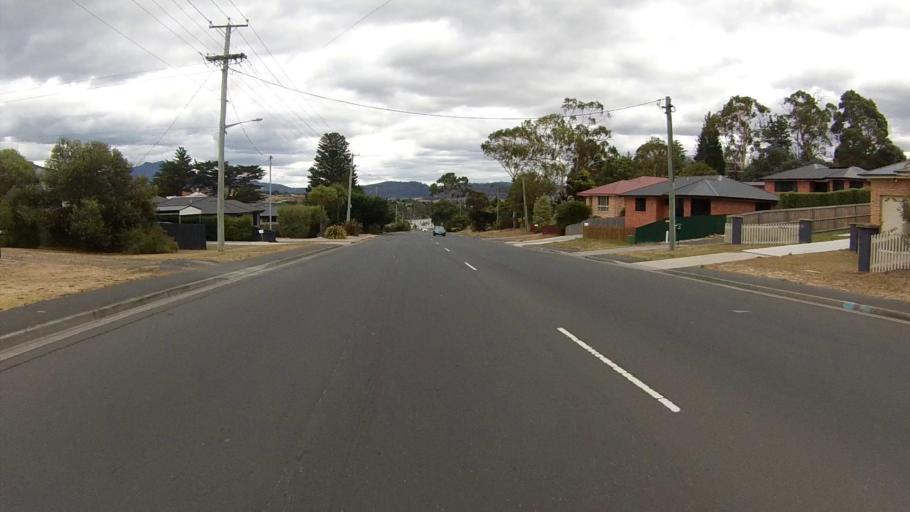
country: AU
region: Tasmania
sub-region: Glenorchy
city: Austins Ferry
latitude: -42.7699
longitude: 147.2463
